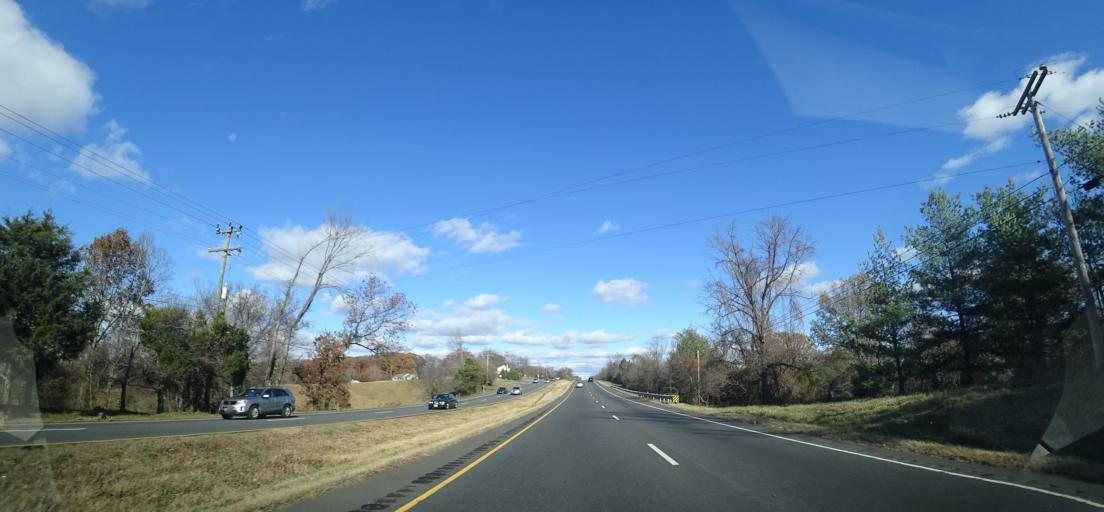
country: US
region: Virginia
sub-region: Fauquier County
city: Warrenton
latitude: 38.6508
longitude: -77.8023
